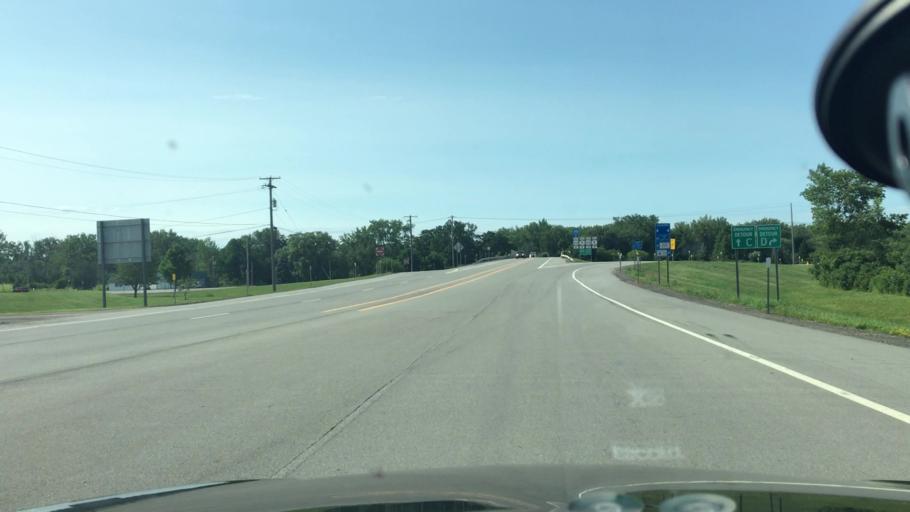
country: US
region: New York
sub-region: Chautauqua County
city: Silver Creek
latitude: 42.5605
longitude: -79.1156
